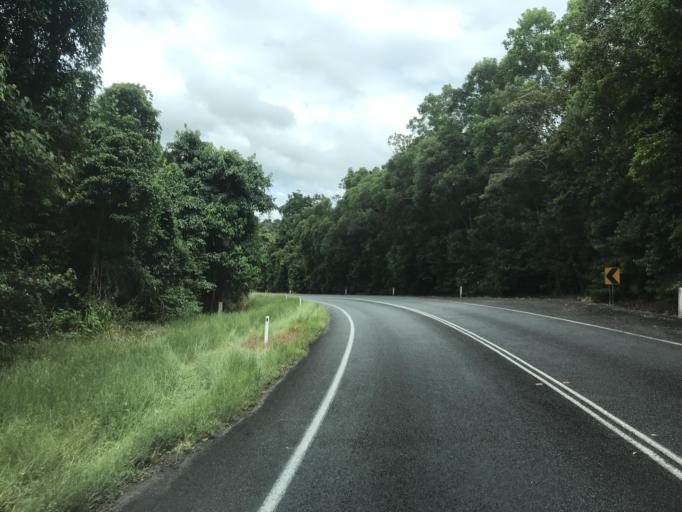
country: AU
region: Queensland
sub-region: Cassowary Coast
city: Innisfail
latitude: -17.8529
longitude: 146.0662
